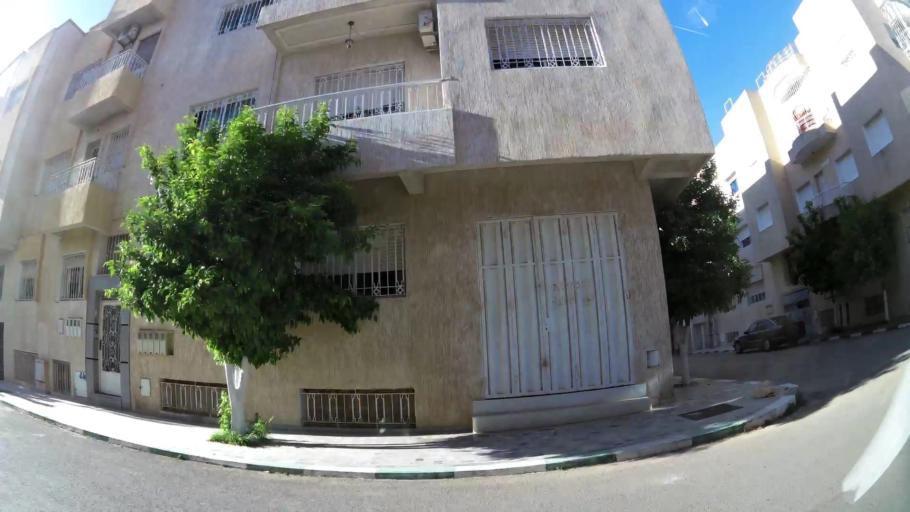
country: MA
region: Fes-Boulemane
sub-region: Fes
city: Fes
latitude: 34.0114
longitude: -5.0122
